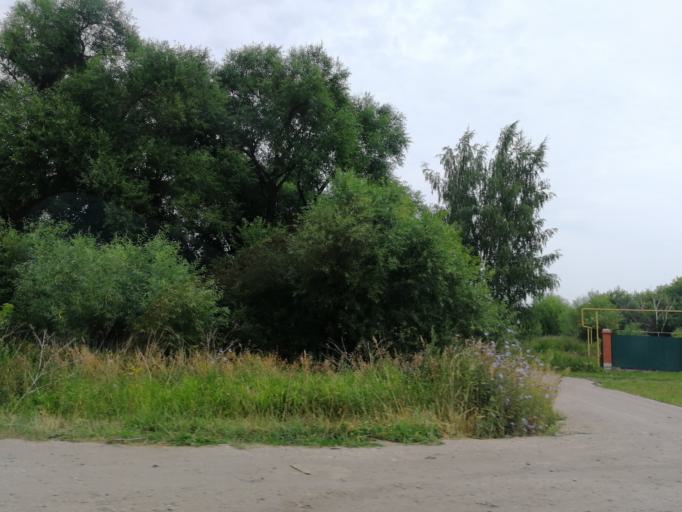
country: RU
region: Tula
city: Bogoroditsk
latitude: 53.7158
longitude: 38.1340
